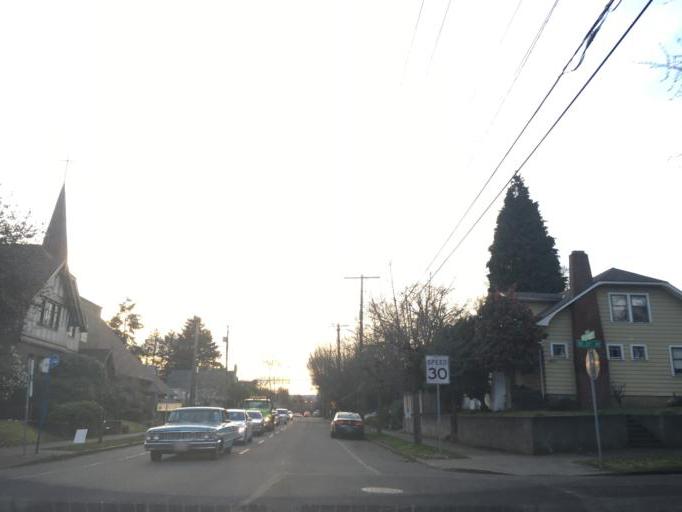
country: US
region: Oregon
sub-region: Multnomah County
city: Portland
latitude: 45.5482
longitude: -122.6379
